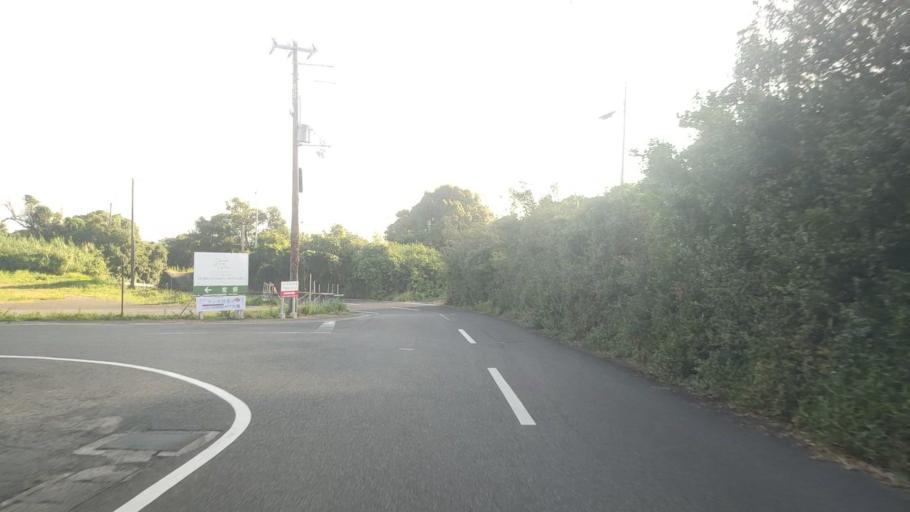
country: JP
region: Wakayama
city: Tanabe
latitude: 33.7780
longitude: 135.3021
